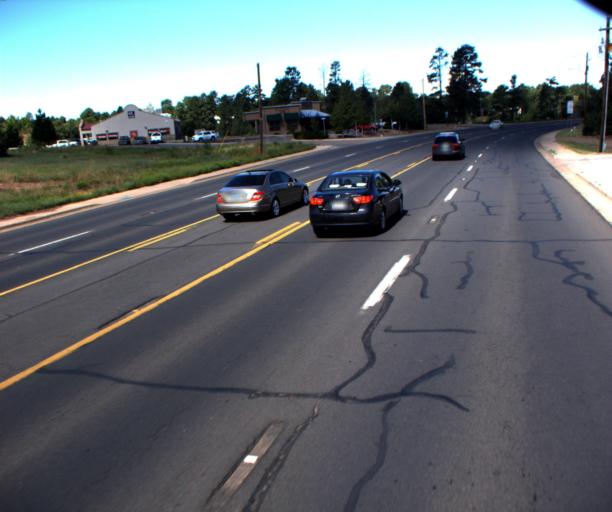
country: US
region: Arizona
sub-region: Navajo County
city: Show Low
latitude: 34.2468
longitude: -110.0262
